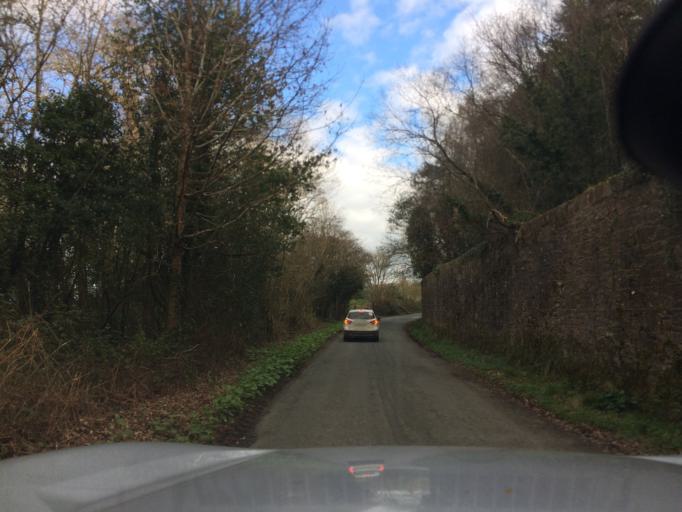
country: IE
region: Munster
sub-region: Waterford
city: Portlaw
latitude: 52.2833
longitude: -7.3200
